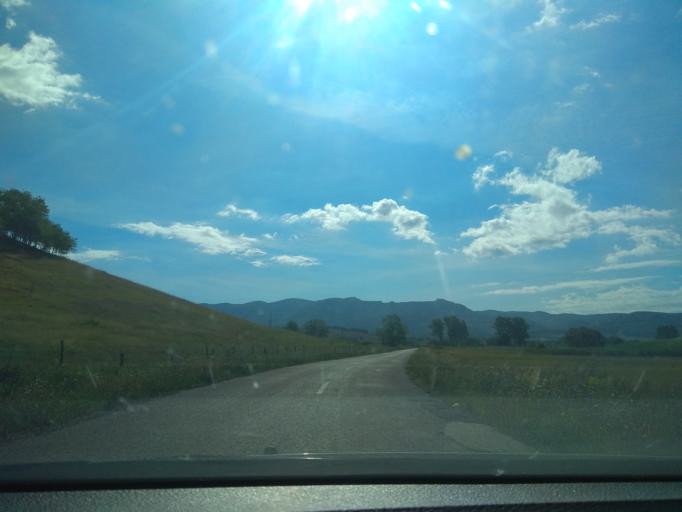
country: HU
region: Heves
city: Belapatfalva
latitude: 48.0702
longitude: 20.3094
